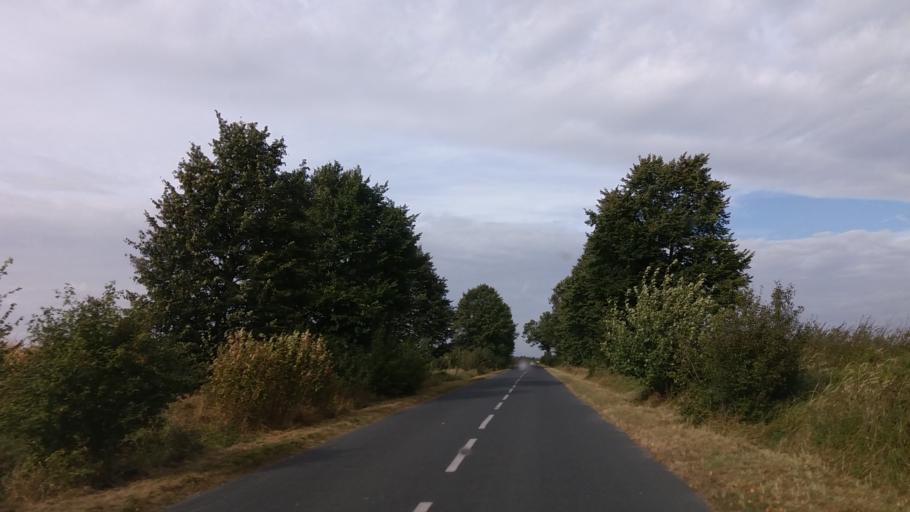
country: PL
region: West Pomeranian Voivodeship
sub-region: Powiat choszczenski
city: Krzecin
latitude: 53.0618
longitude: 15.4923
